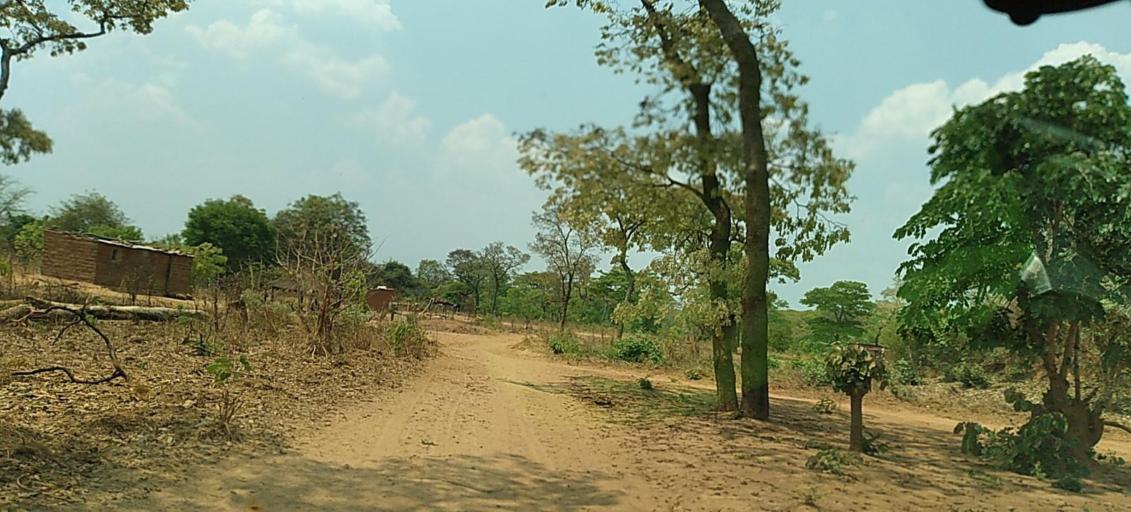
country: ZM
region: North-Western
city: Kabompo
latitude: -13.6431
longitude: 24.3792
